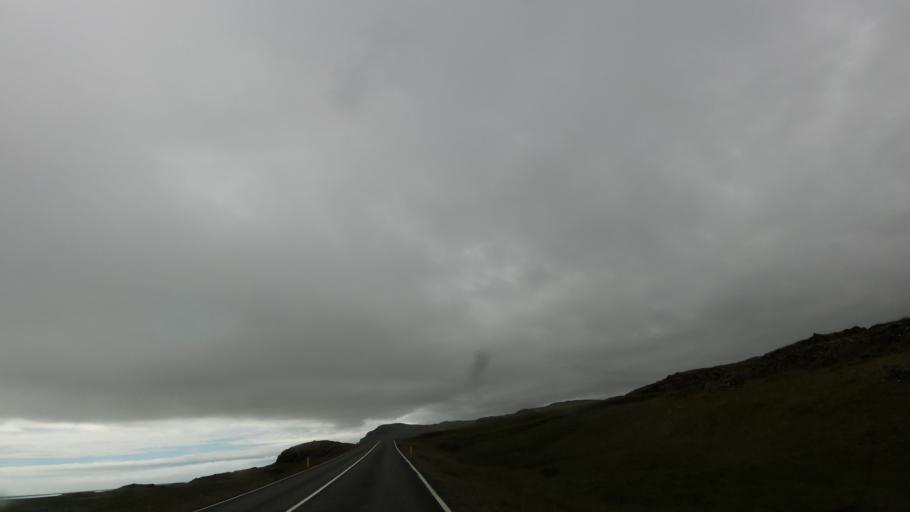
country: IS
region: East
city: Hoefn
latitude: 64.2269
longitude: -15.6872
